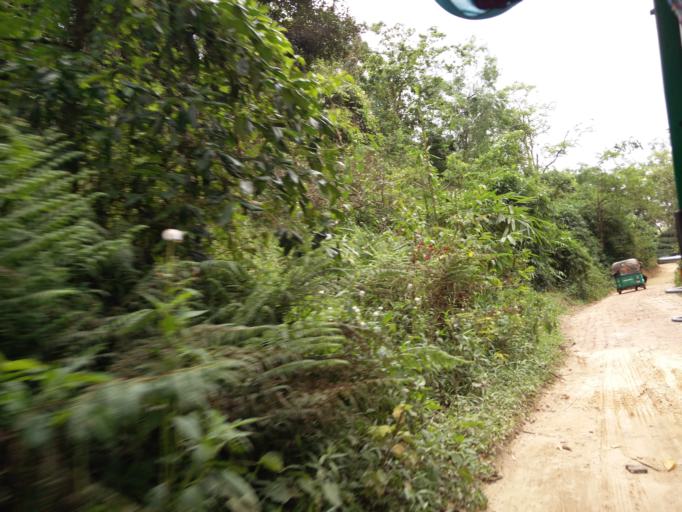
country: IN
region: Tripura
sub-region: Dhalai
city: Kamalpur
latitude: 24.3030
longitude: 91.7909
